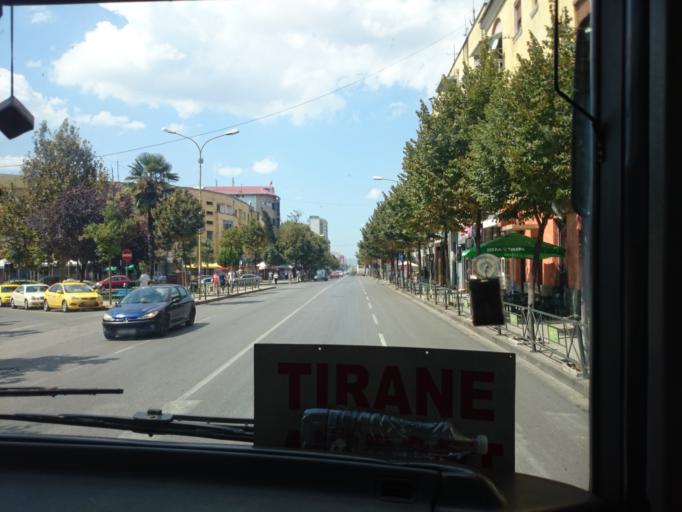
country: AL
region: Tirane
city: Tirana
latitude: 41.3318
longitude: 19.8081
